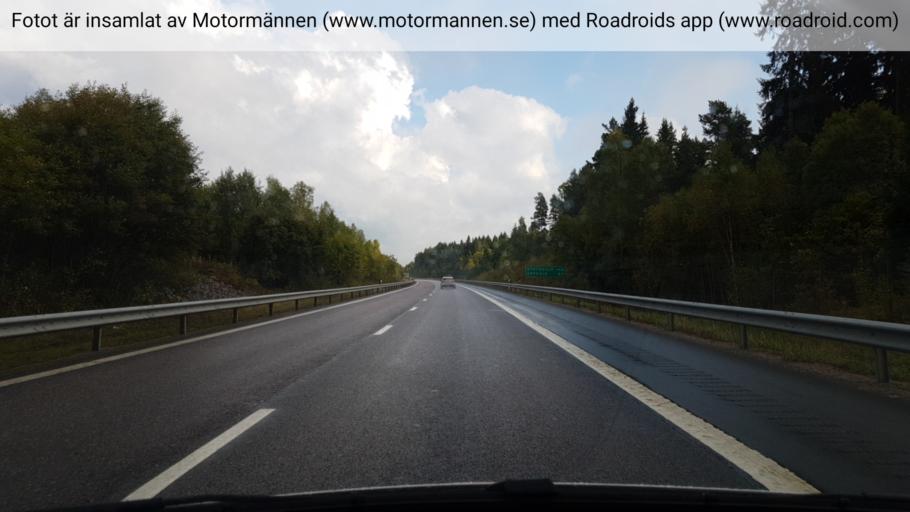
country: SE
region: Uppsala
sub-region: Alvkarleby Kommun
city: AElvkarleby
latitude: 60.4970
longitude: 17.3233
